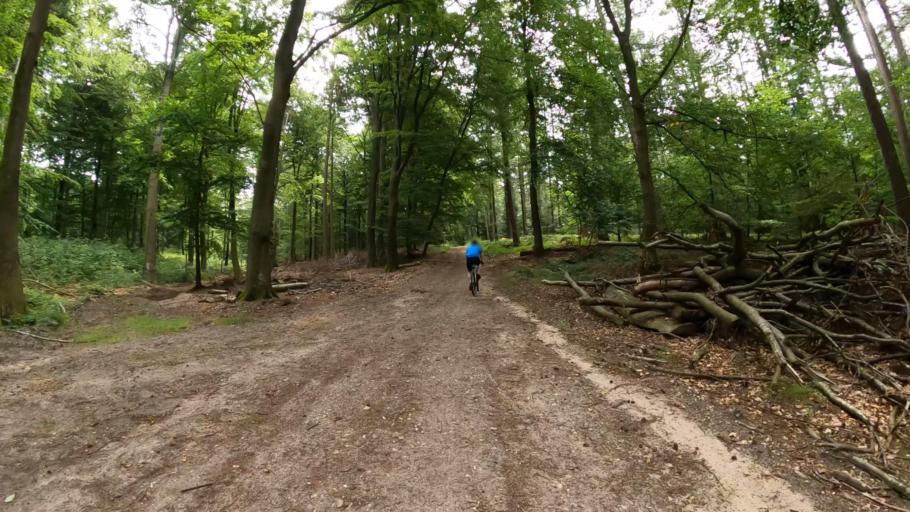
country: DE
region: Schleswig-Holstein
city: Heidmuhlen
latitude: 53.9579
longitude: 10.1021
